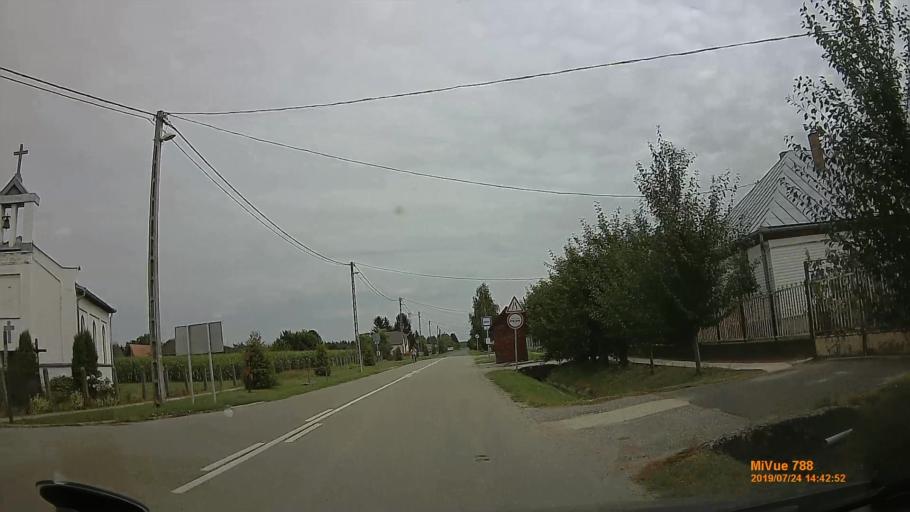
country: HU
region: Szabolcs-Szatmar-Bereg
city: Mandok
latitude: 48.3144
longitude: 22.2732
